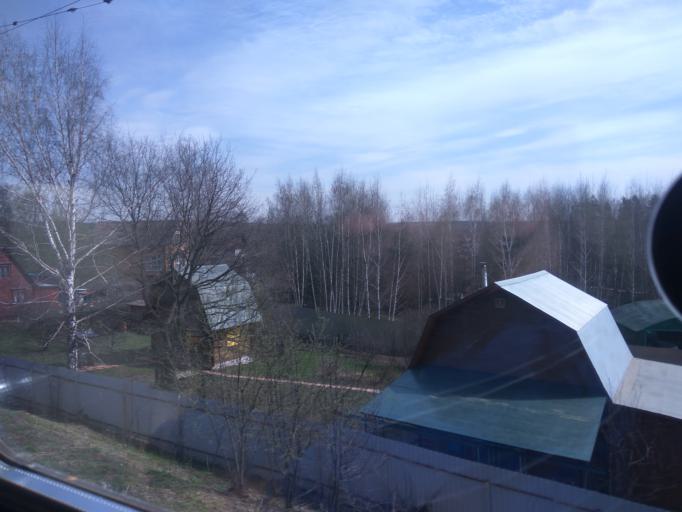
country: RU
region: Moskovskaya
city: Yermolino
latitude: 56.1446
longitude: 37.5068
